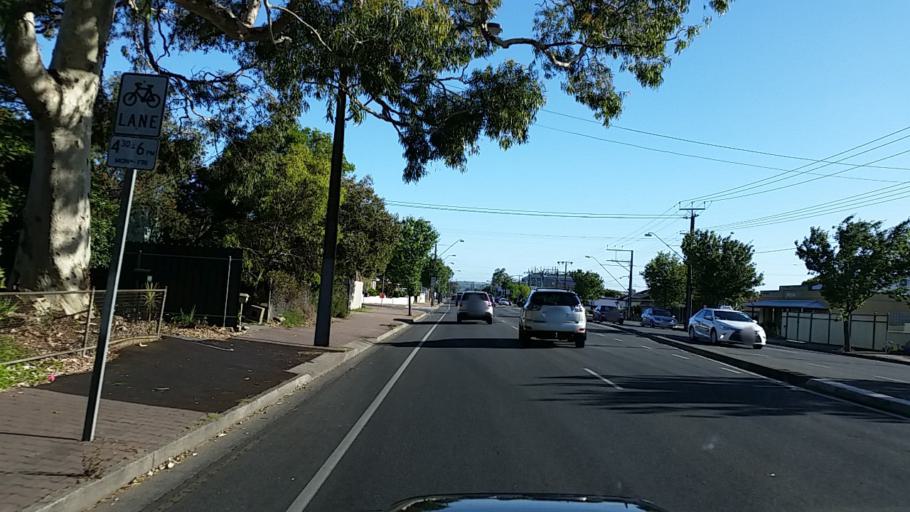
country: AU
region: South Australia
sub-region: Marion
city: South Plympton
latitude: -34.9748
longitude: 138.5556
